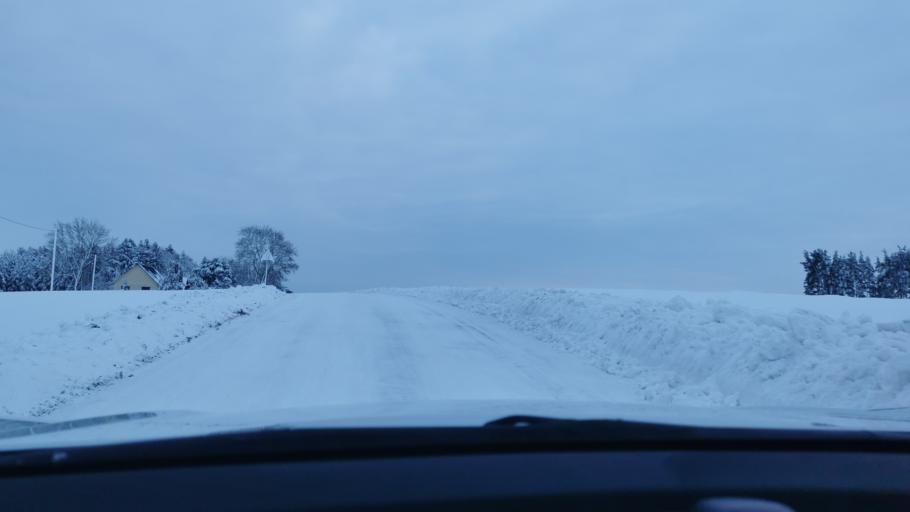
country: EE
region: Laeaene-Virumaa
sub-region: Viru-Nigula vald
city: Kunda
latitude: 59.4246
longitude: 26.5086
